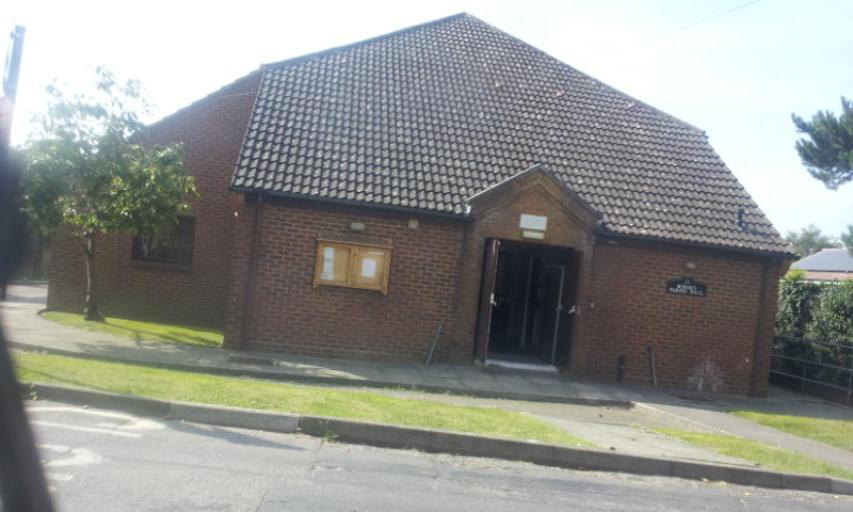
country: GB
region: England
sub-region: Kent
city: Sittingbourne
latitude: 51.3352
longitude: 0.6998
